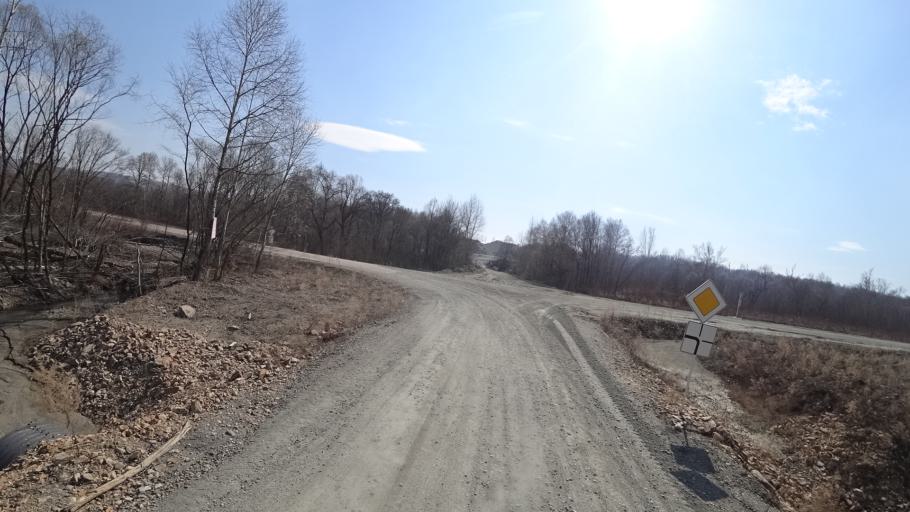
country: RU
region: Amur
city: Novobureyskiy
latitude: 49.7970
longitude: 129.9572
